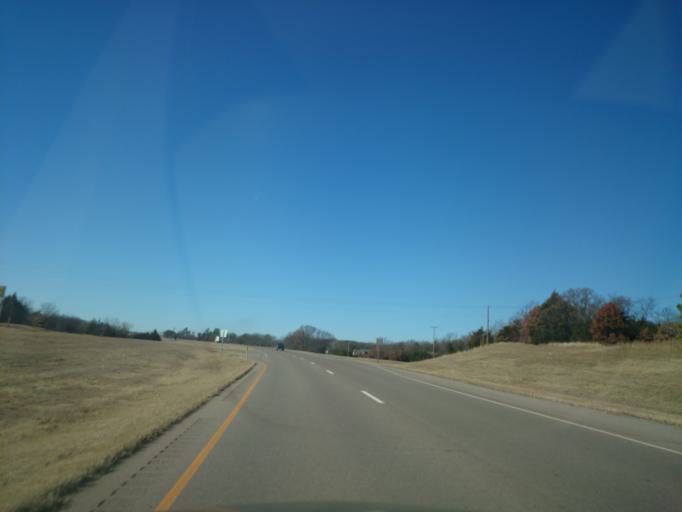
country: US
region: Oklahoma
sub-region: Payne County
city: Stillwater
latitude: 36.1163
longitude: -97.1837
